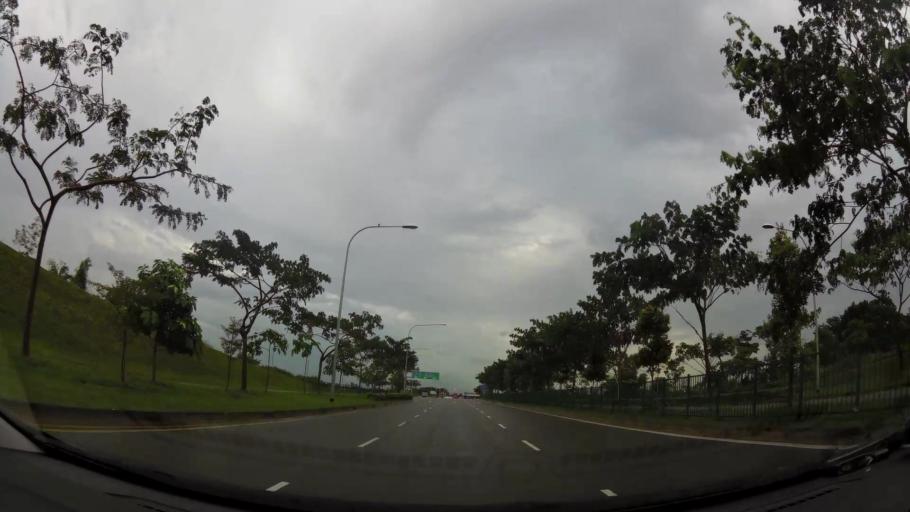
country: MY
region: Johor
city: Kampung Pasir Gudang Baru
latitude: 1.3985
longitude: 103.8689
